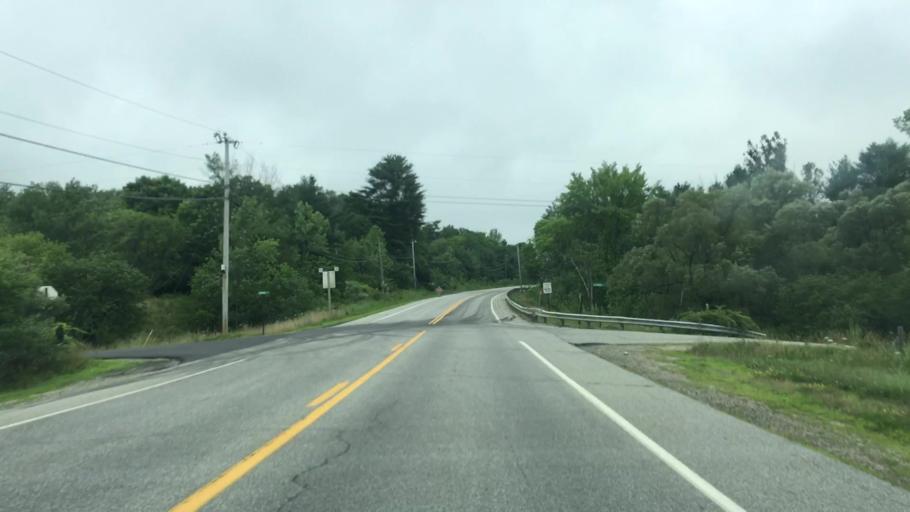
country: US
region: Maine
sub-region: Sagadahoc County
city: Richmond
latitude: 44.1105
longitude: -69.7289
